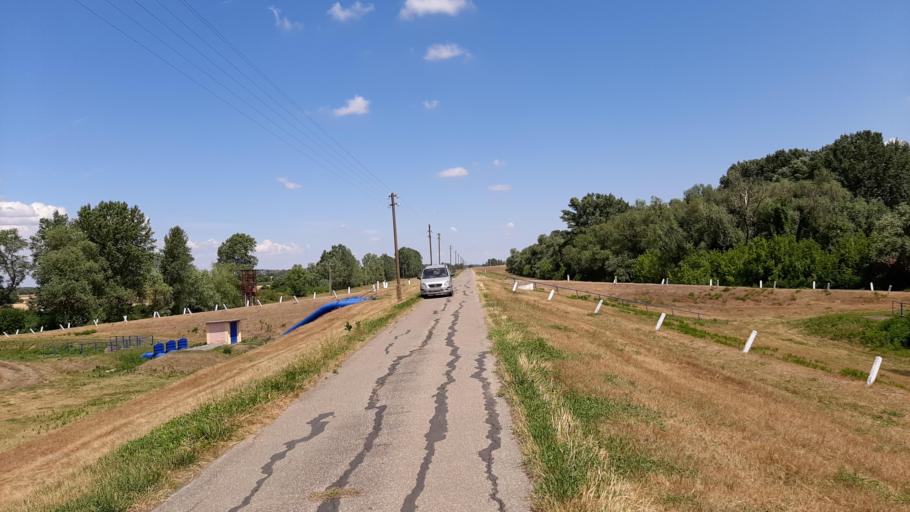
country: HU
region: Csongrad
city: Csanytelek
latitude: 46.5791
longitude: 20.1367
